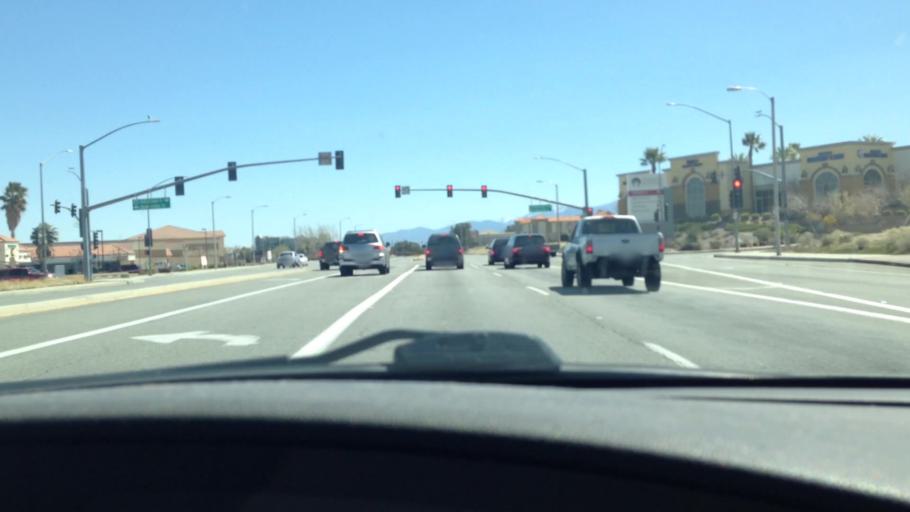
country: US
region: California
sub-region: Los Angeles County
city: Desert View Highlands
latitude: 34.5859
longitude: -118.1443
